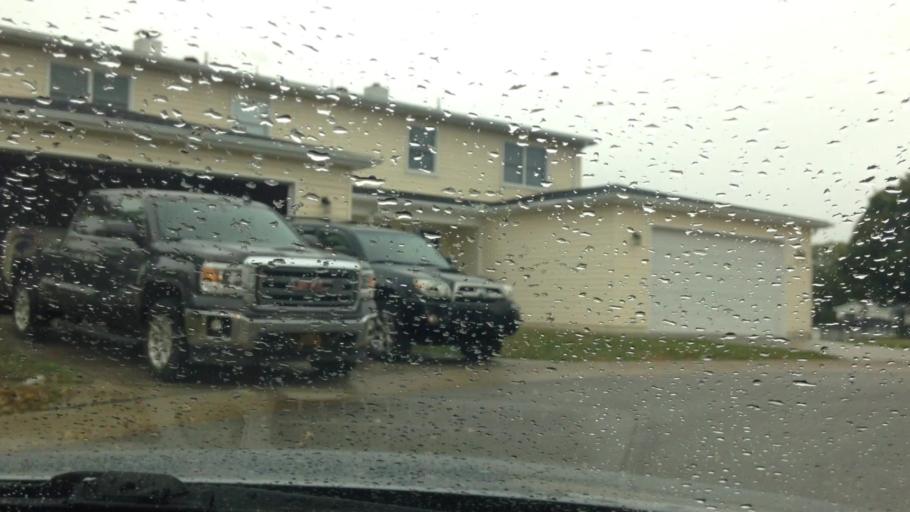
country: US
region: Kansas
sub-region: Leavenworth County
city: Leavenworth
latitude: 39.3416
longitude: -94.9346
